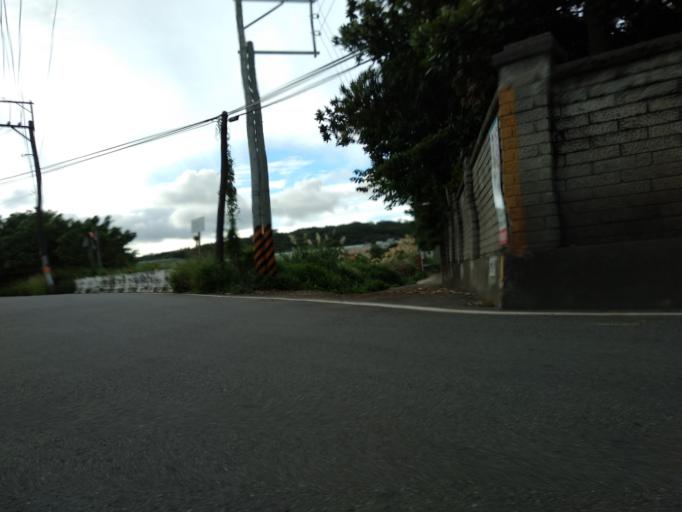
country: TW
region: Taiwan
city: Daxi
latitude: 24.9237
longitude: 121.1932
